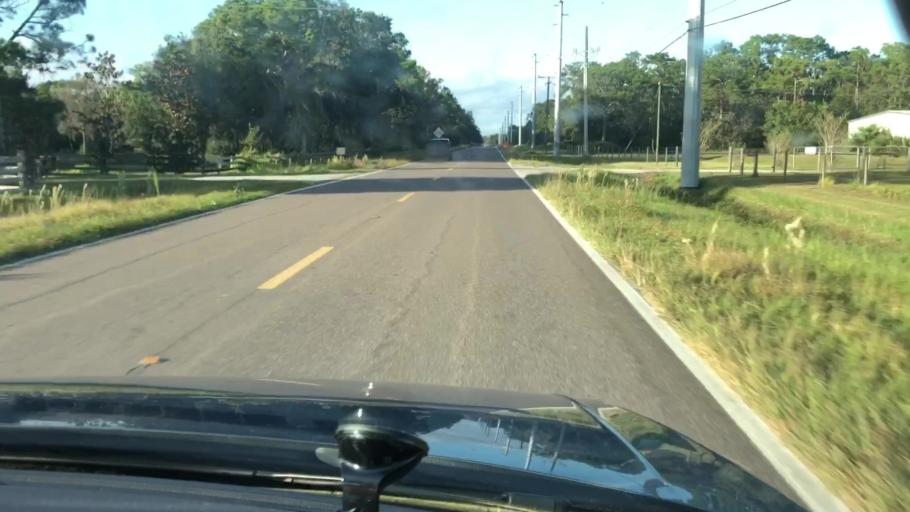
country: US
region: Florida
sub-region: Polk County
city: Polk City
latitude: 28.1482
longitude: -81.8973
